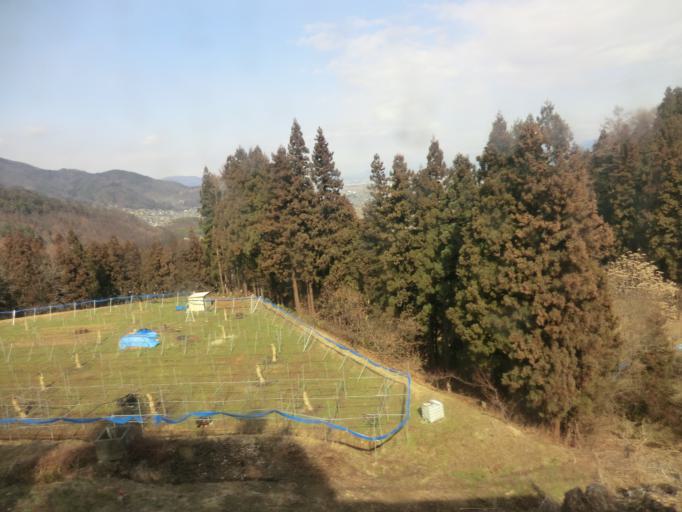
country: JP
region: Nagano
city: Nagano-shi
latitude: 36.5090
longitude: 138.0825
